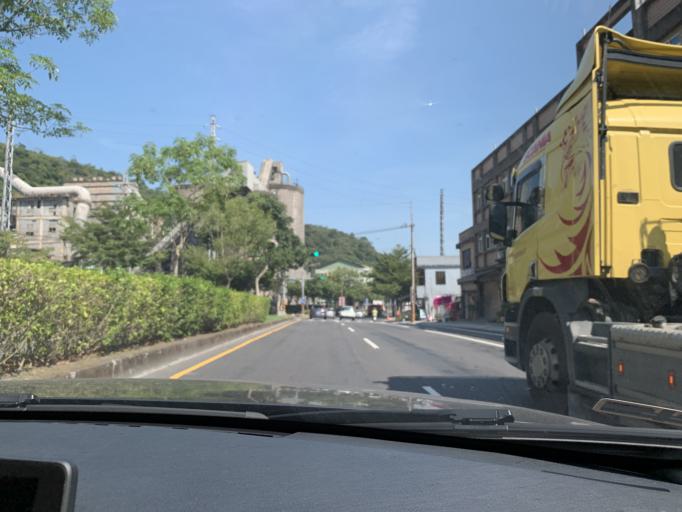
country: TW
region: Taiwan
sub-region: Yilan
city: Yilan
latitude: 24.6076
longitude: 121.8274
